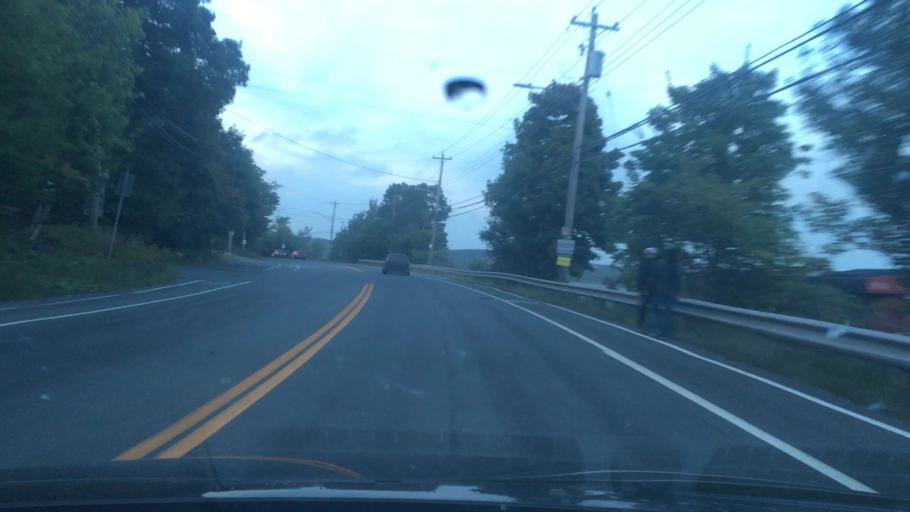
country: CA
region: Nova Scotia
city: Dartmouth
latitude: 44.6861
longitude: -63.6594
